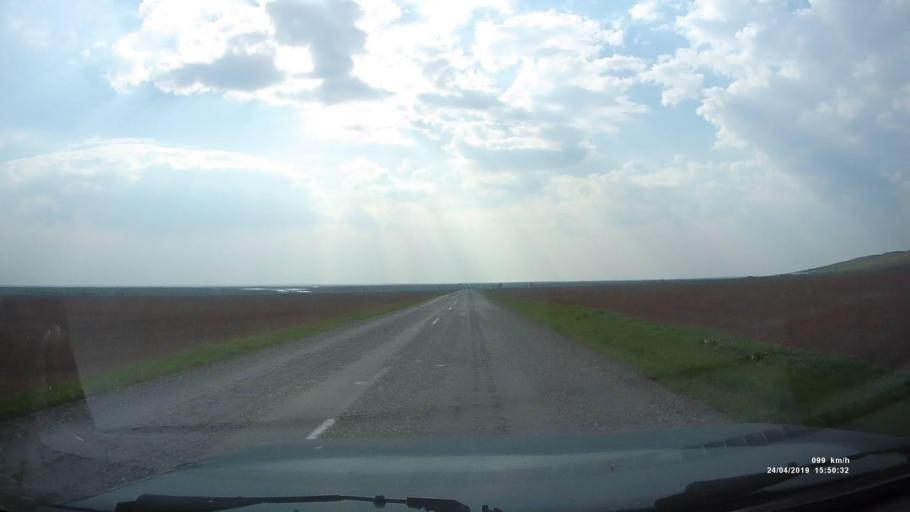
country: RU
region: Kalmykiya
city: Yashalta
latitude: 46.6041
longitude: 42.6308
